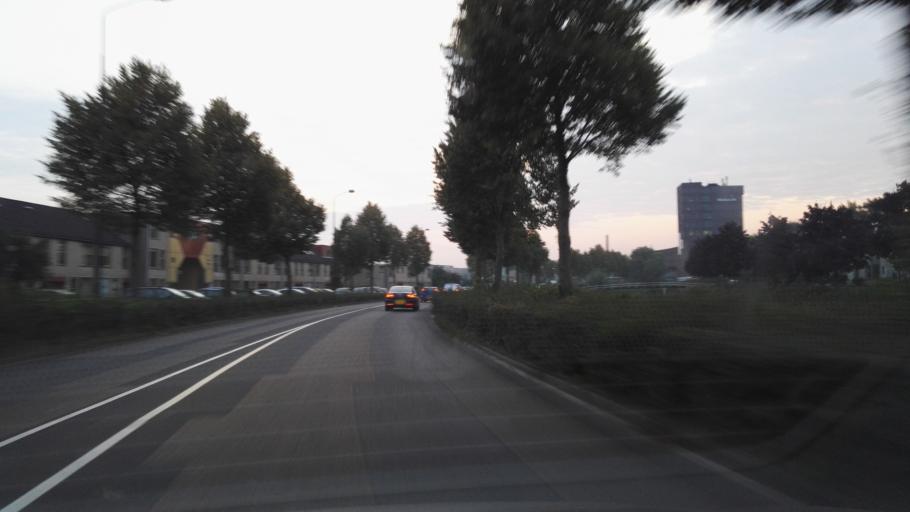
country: NL
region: Gelderland
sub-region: Gemeente Apeldoorn
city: Apeldoorn
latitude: 52.2109
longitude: 5.9836
